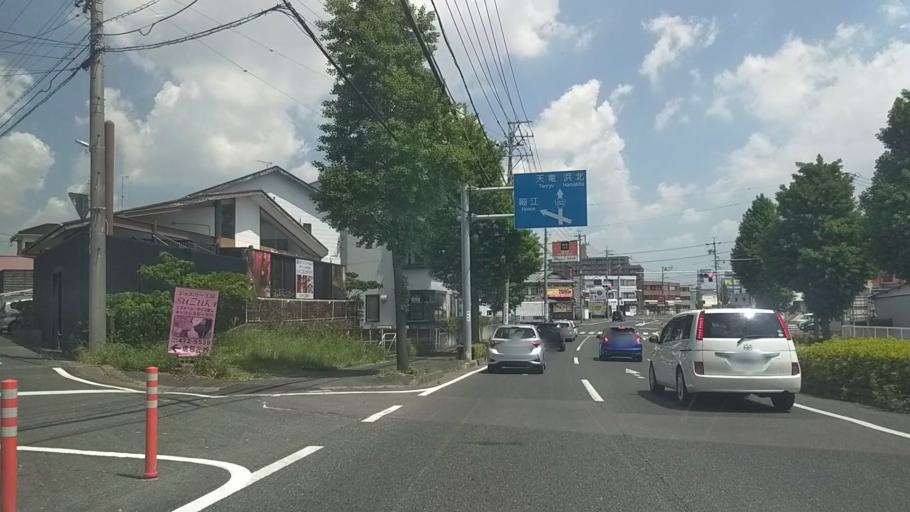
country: JP
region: Shizuoka
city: Hamamatsu
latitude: 34.7437
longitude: 137.7403
